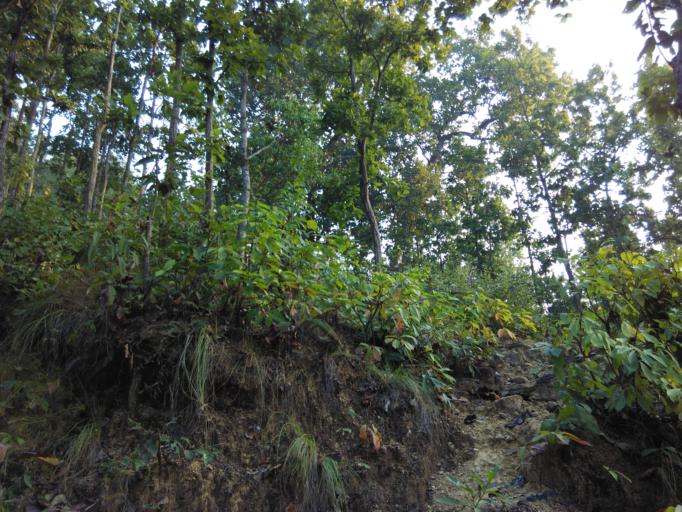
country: NP
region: Central Region
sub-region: Narayani Zone
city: Bharatpur
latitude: 27.7216
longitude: 84.4183
